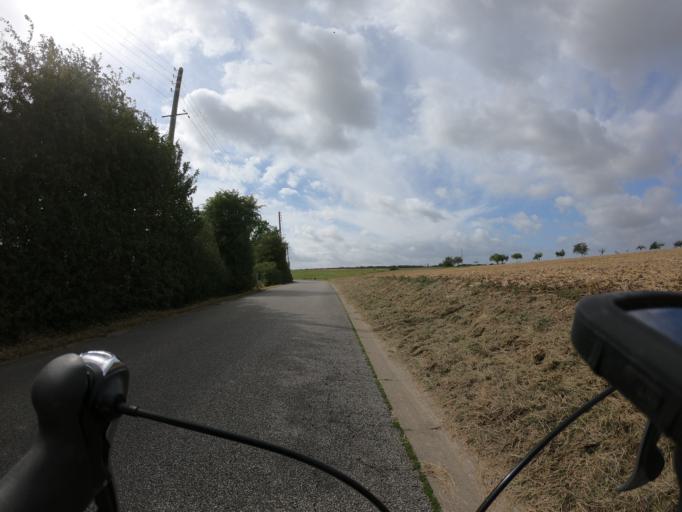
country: FR
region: Ile-de-France
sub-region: Departement des Yvelines
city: Magny-les-Hameaux
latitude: 48.7443
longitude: 2.0548
